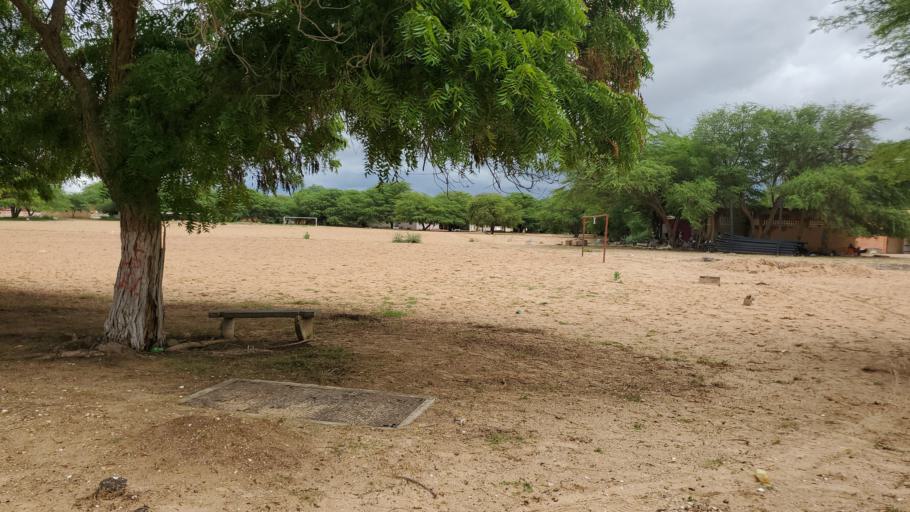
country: SN
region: Saint-Louis
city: Saint-Louis
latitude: 16.0665
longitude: -16.4259
